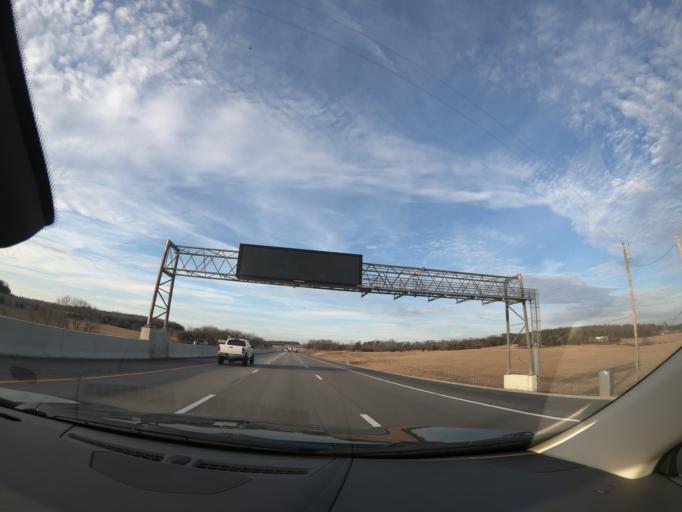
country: US
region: Kentucky
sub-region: Hart County
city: Munfordville
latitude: 37.4275
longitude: -85.8829
